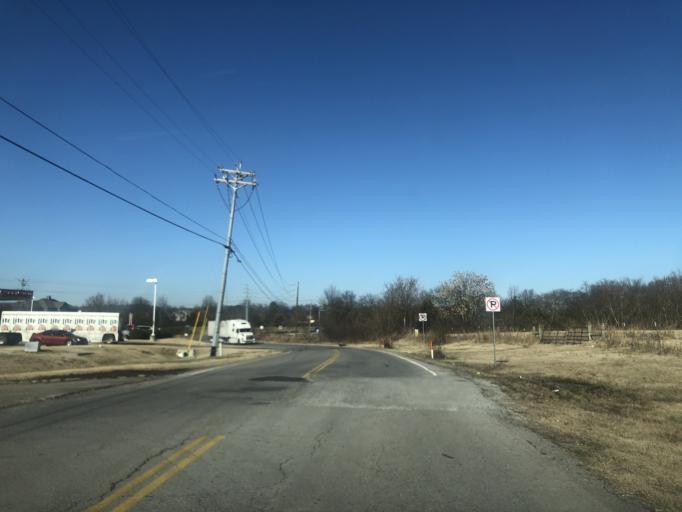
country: US
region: Tennessee
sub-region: Rutherford County
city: Smyrna
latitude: 35.9352
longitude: -86.5289
